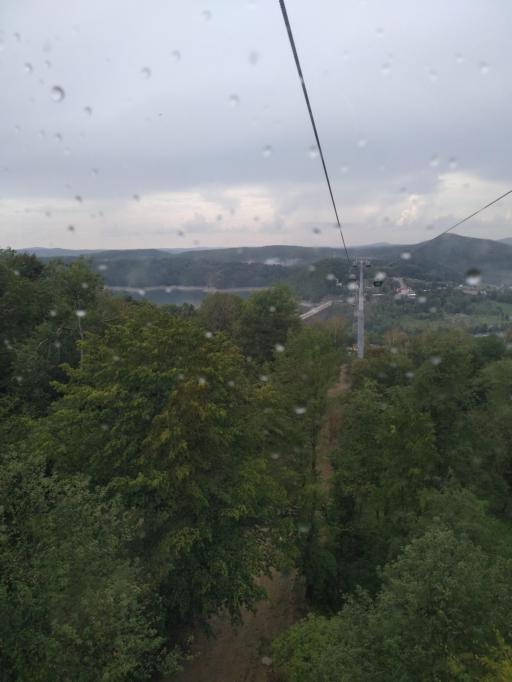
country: PL
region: Subcarpathian Voivodeship
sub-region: Powiat leski
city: Polanczyk
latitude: 49.3926
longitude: 22.4669
